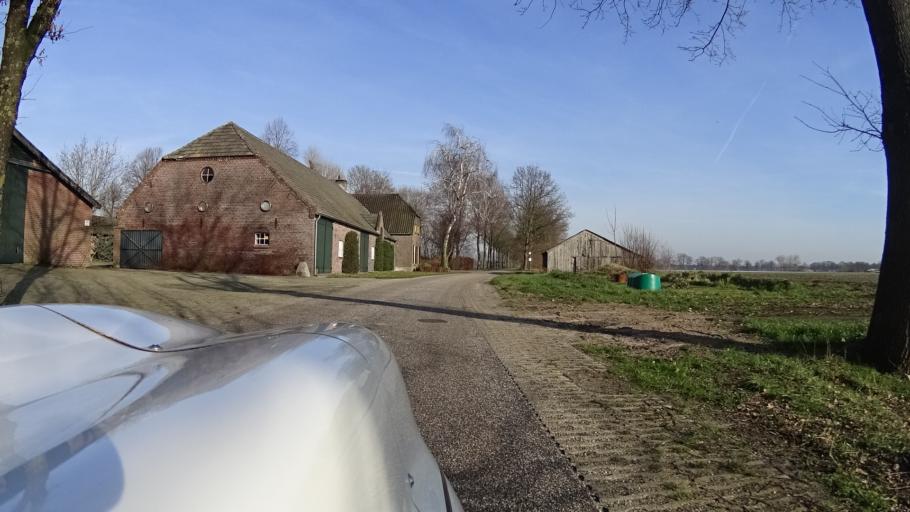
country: NL
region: North Brabant
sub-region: Gemeente Boekel
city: Boekel
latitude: 51.5799
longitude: 5.6684
